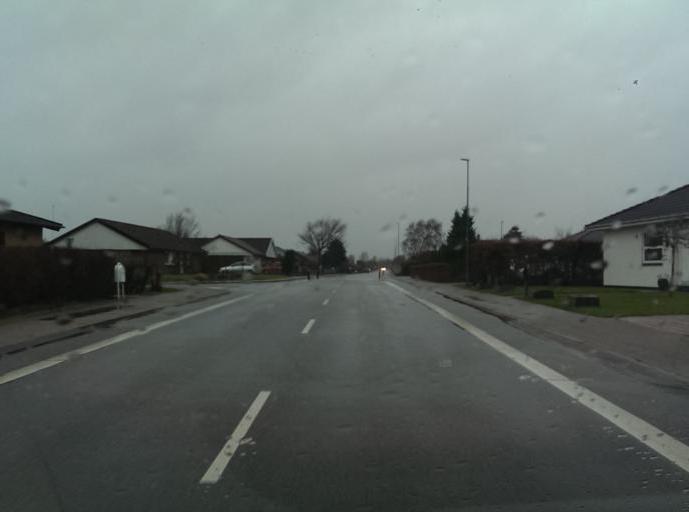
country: DK
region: South Denmark
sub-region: Esbjerg Kommune
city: Esbjerg
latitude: 55.5014
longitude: 8.4433
